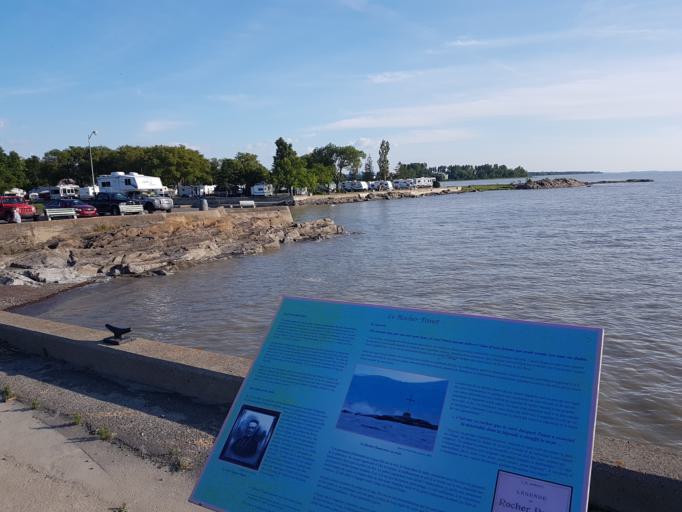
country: CA
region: Quebec
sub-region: Chaudiere-Appalaches
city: Montmagny
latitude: 47.1341
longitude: -70.3703
